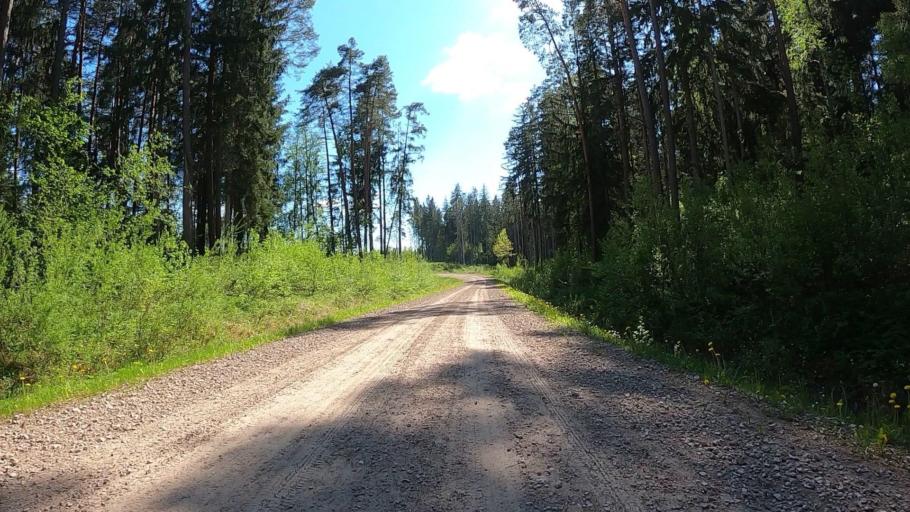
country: LV
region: Baldone
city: Baldone
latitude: 56.7866
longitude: 24.3411
